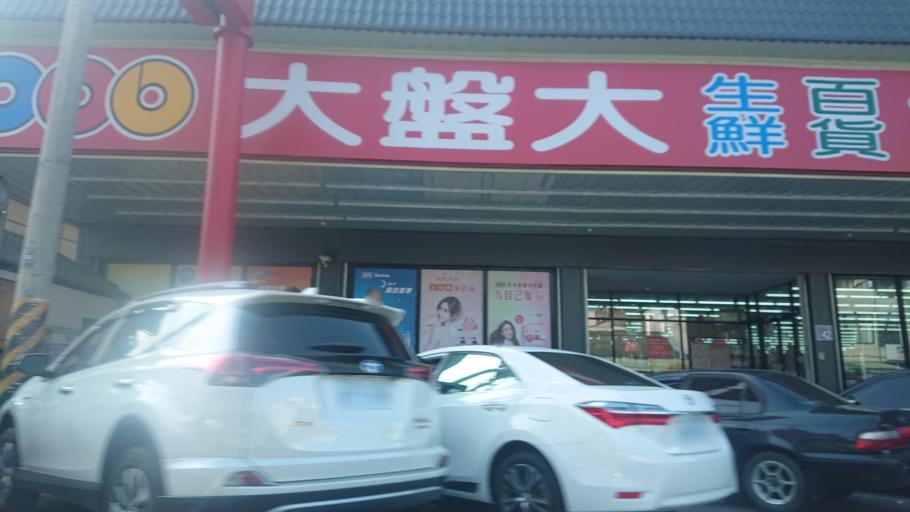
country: TW
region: Taiwan
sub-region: Chiayi
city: Taibao
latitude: 23.4624
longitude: 120.2411
